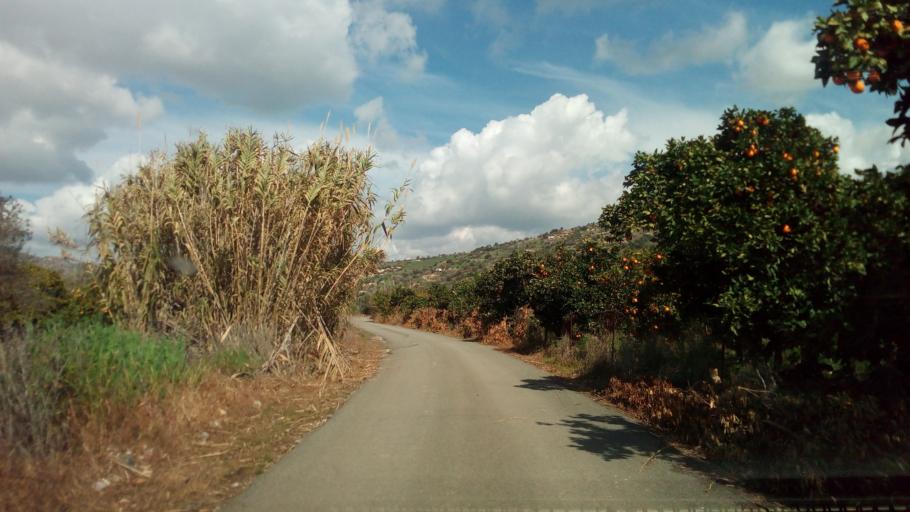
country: CY
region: Pafos
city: Mesogi
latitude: 34.8019
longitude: 32.5296
